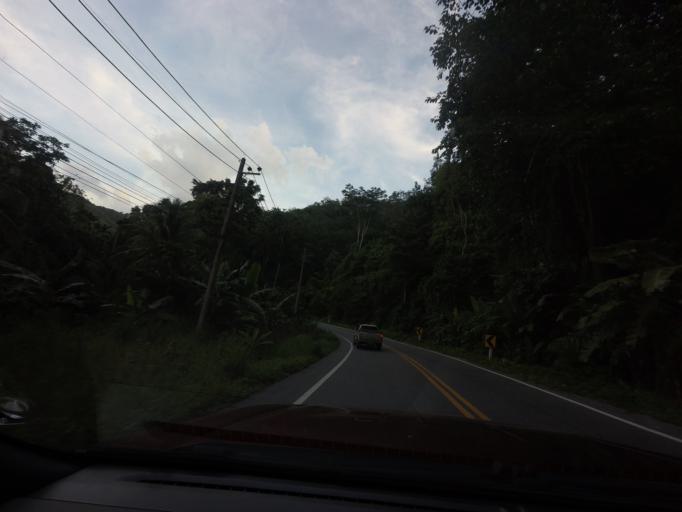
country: TH
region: Yala
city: Than To
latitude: 6.0376
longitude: 101.1960
